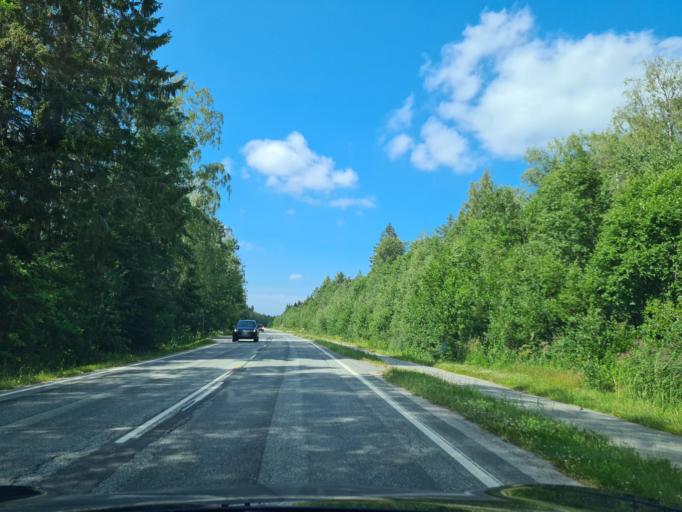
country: FI
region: Ostrobothnia
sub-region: Vaasa
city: Vaasa
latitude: 63.1972
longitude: 21.5428
